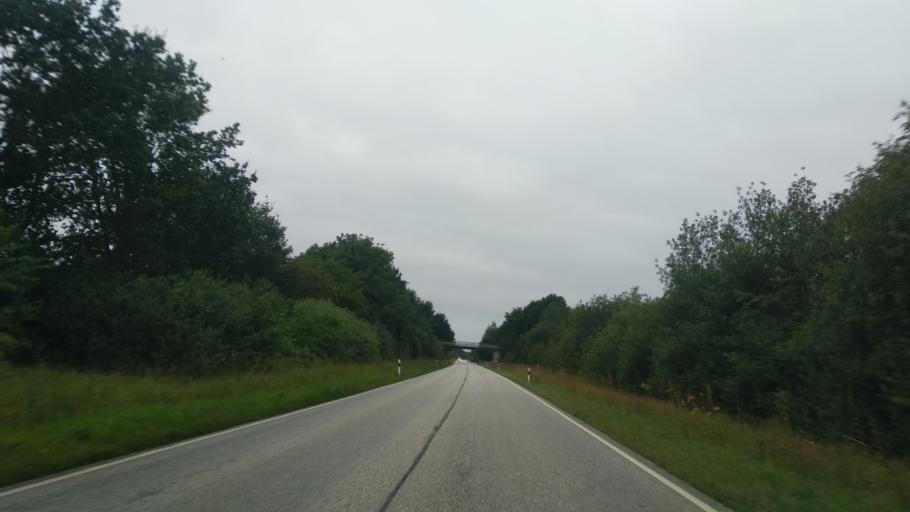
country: DE
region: Schleswig-Holstein
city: Lurschau
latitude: 54.5431
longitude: 9.4999
